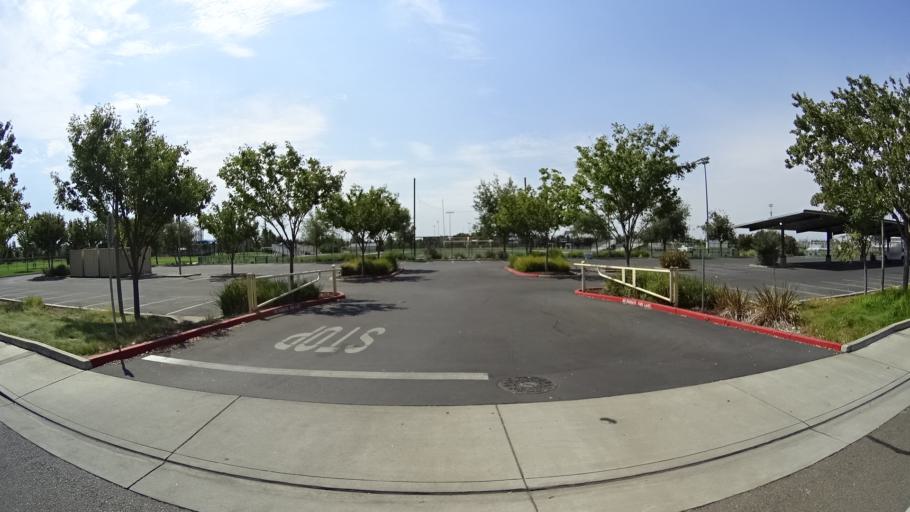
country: US
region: California
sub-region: Sacramento County
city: Laguna
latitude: 38.3940
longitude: -121.4252
